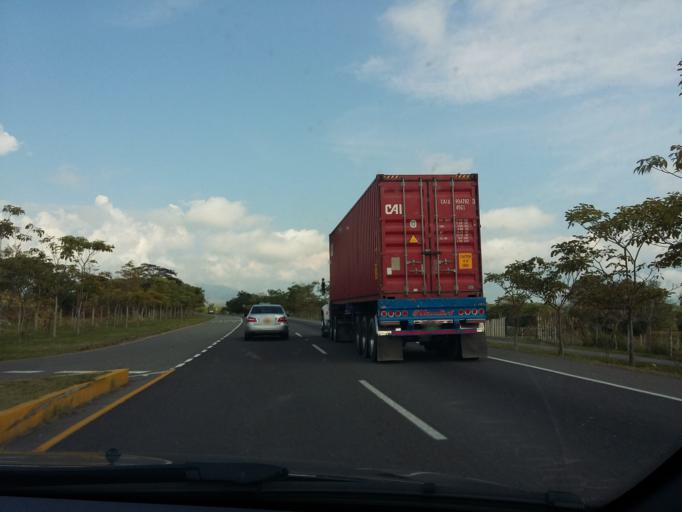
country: CO
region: Tolima
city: Ibague
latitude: 4.3668
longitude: -75.1351
